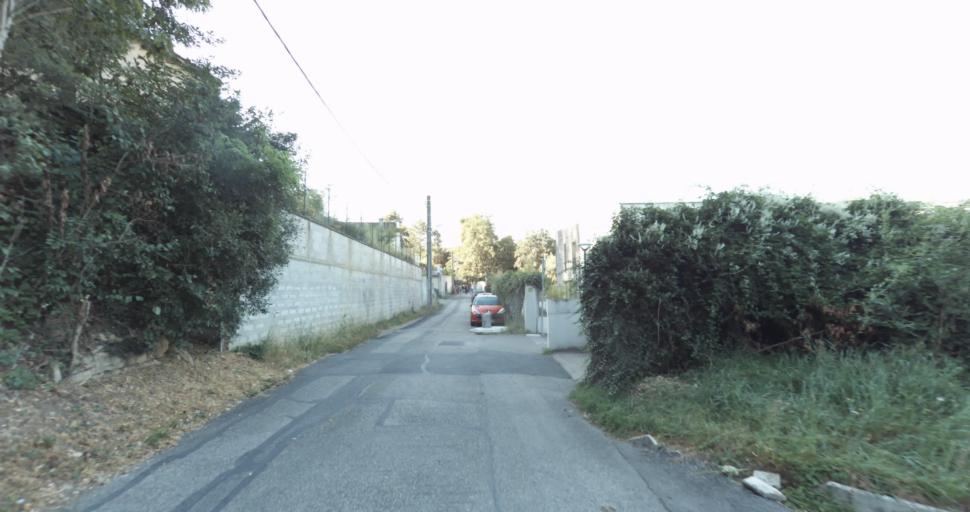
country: FR
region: Rhone-Alpes
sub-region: Departement du Rhone
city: Neuville-sur-Saone
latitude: 45.8825
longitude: 4.8521
